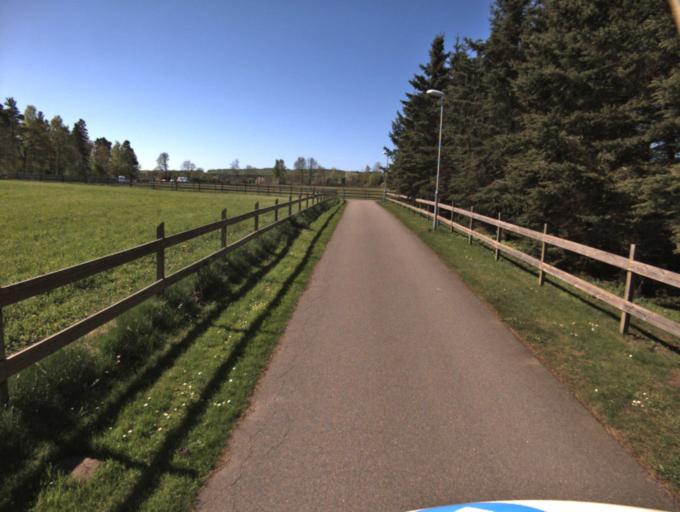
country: SE
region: Skane
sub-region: Kristianstads Kommun
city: Onnestad
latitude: 55.9276
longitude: 13.9852
